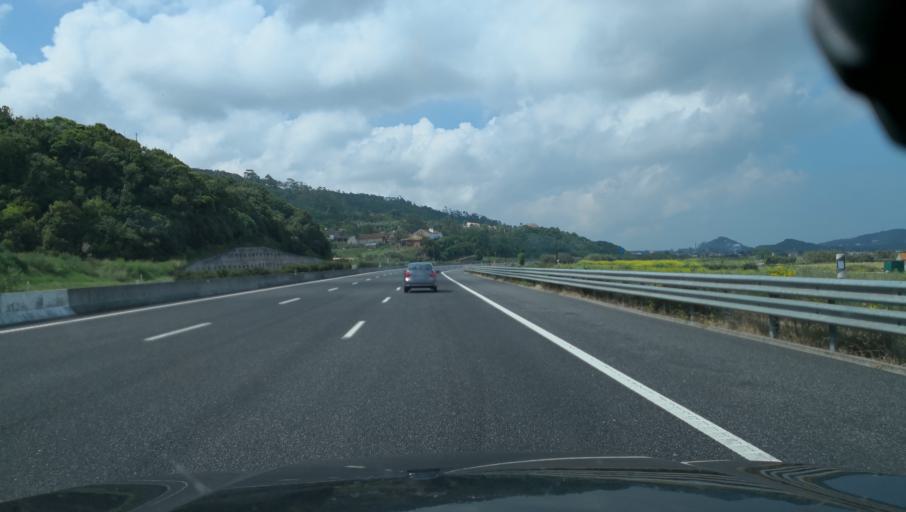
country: PT
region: Leiria
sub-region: Nazare
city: Nazare
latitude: 39.5595
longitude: -9.0446
